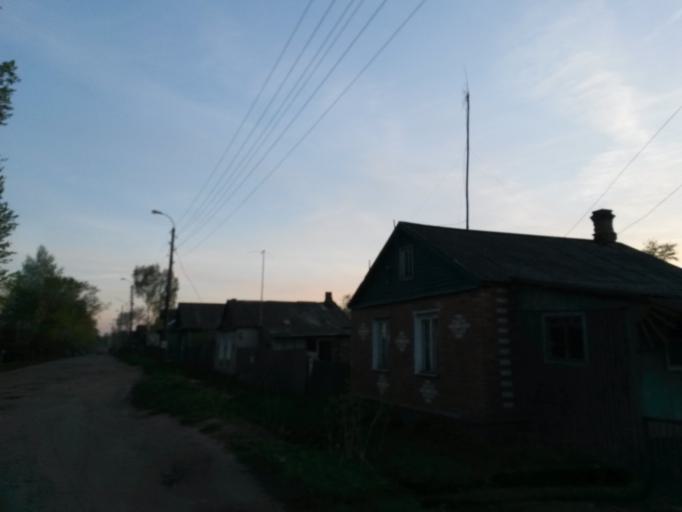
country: RU
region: Jaroslavl
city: Tutayev
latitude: 57.8877
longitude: 39.5522
